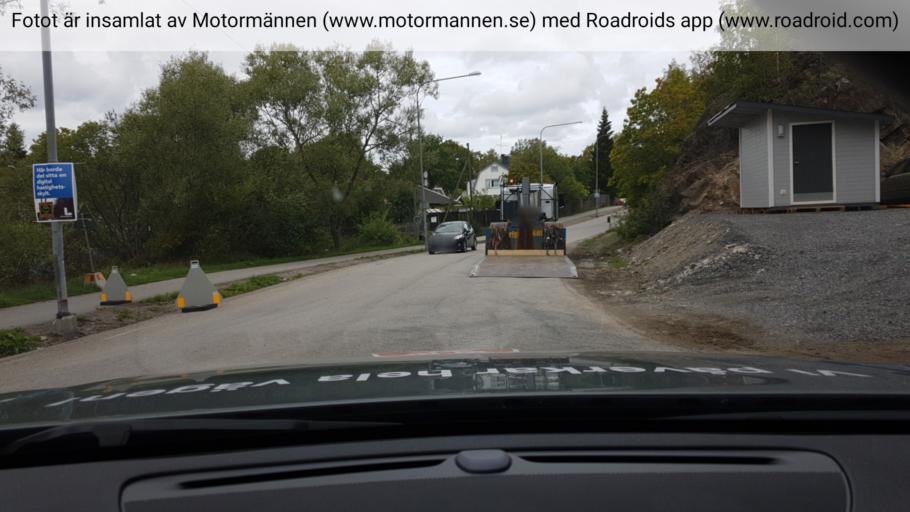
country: SE
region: Stockholm
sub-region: Huddinge Kommun
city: Huddinge
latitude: 59.2345
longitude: 17.9963
